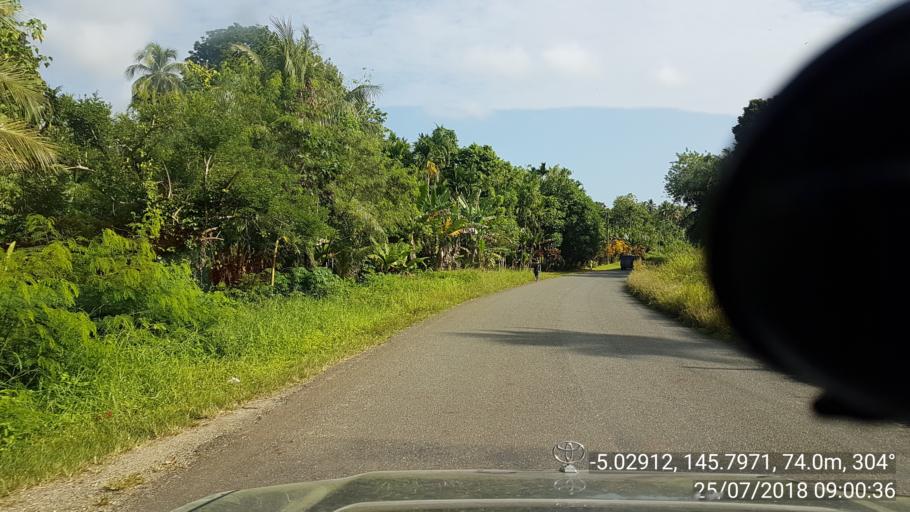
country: PG
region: Madang
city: Madang
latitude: -5.0292
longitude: 145.7972
